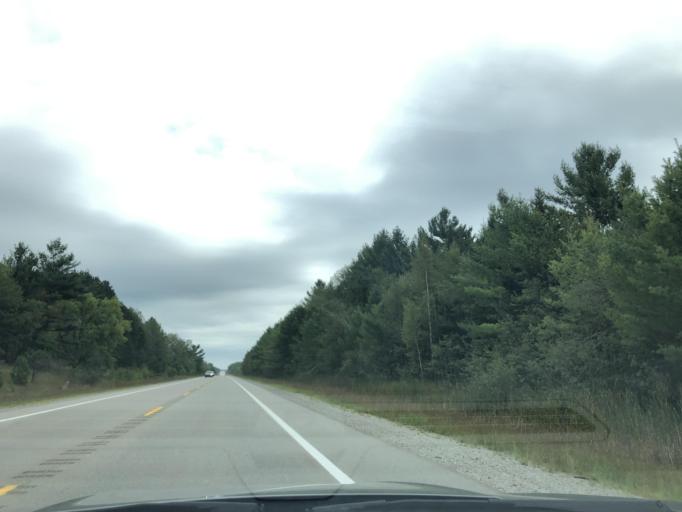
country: US
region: Michigan
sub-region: Clare County
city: Harrison
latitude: 44.0311
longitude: -84.9862
